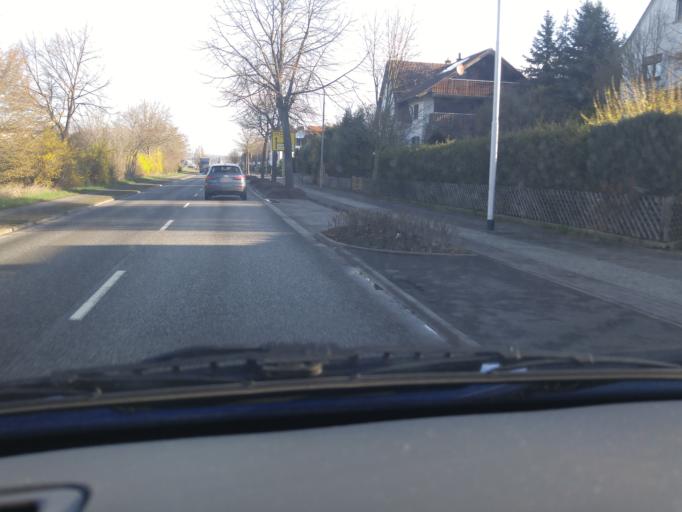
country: DE
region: Hesse
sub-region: Regierungsbezirk Giessen
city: Lauterbach
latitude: 50.6236
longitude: 9.3936
